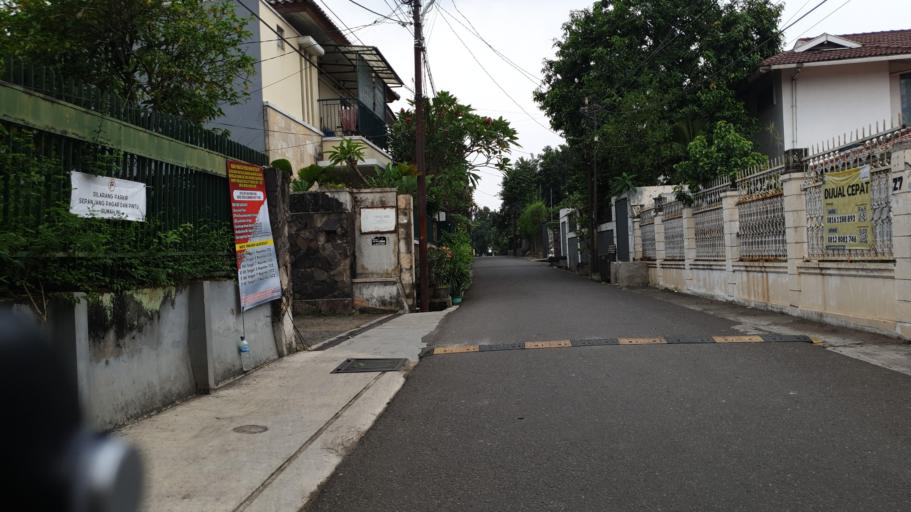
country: ID
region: Jakarta Raya
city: Jakarta
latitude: -6.2736
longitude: 106.7949
